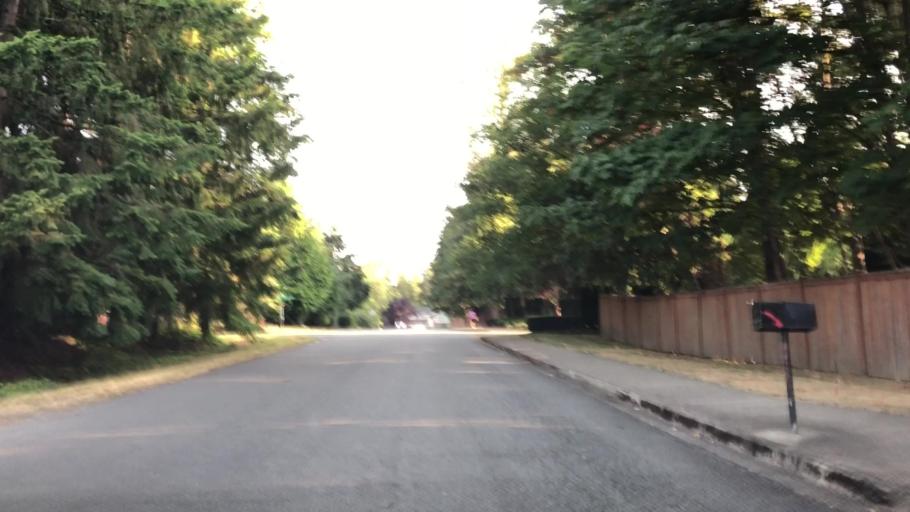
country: US
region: Washington
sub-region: King County
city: Cottage Lake
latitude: 47.7197
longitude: -122.1021
